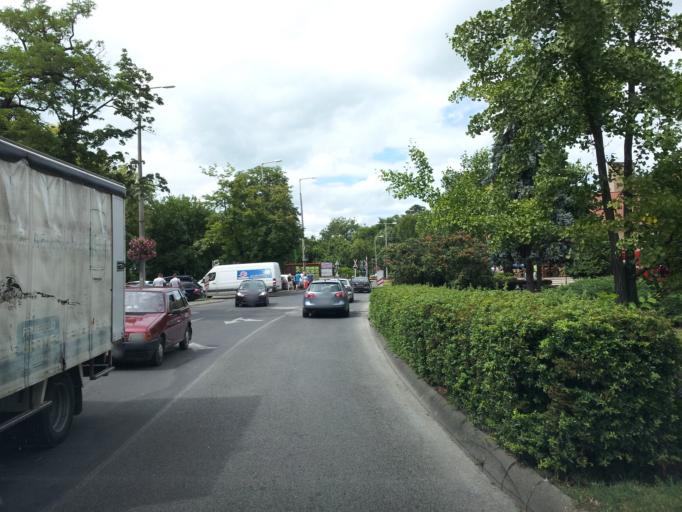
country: HU
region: Somogy
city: Siofok
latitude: 46.9054
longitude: 18.0490
